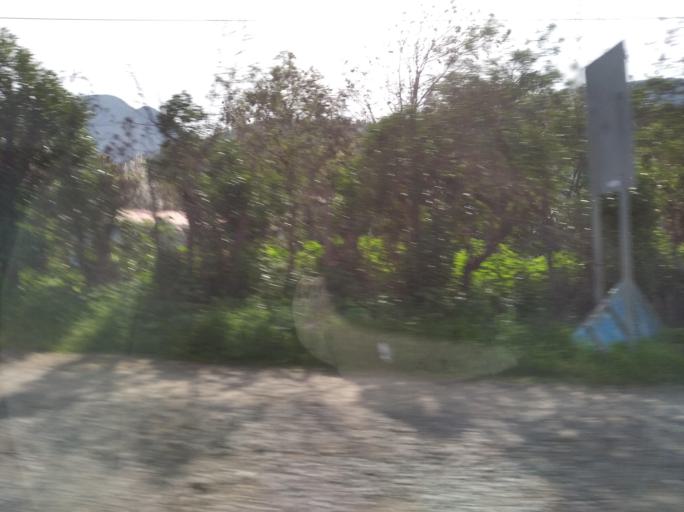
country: CL
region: Valparaiso
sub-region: Provincia de Marga Marga
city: Limache
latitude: -33.0526
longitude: -71.0964
